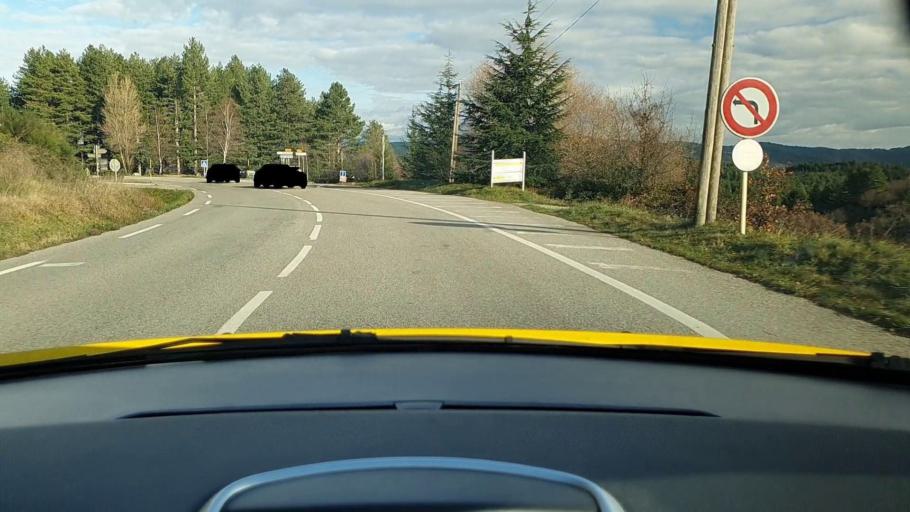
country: FR
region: Languedoc-Roussillon
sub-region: Departement du Gard
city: Branoux-les-Taillades
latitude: 44.3777
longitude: 3.9422
